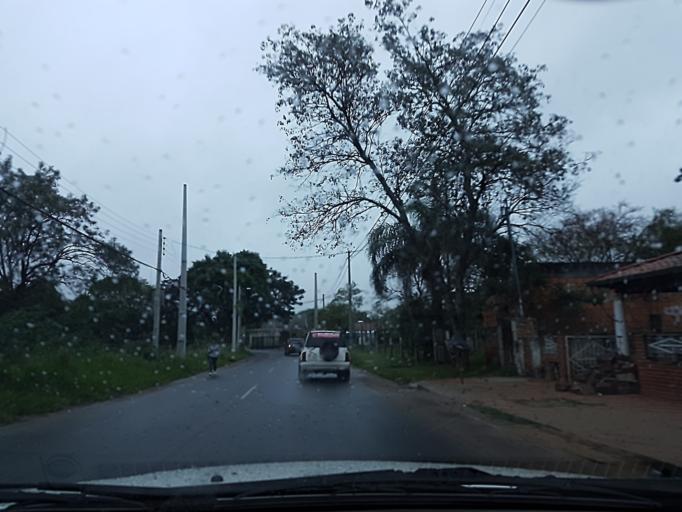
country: PY
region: Central
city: Colonia Mariano Roque Alonso
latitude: -25.2212
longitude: -57.5430
